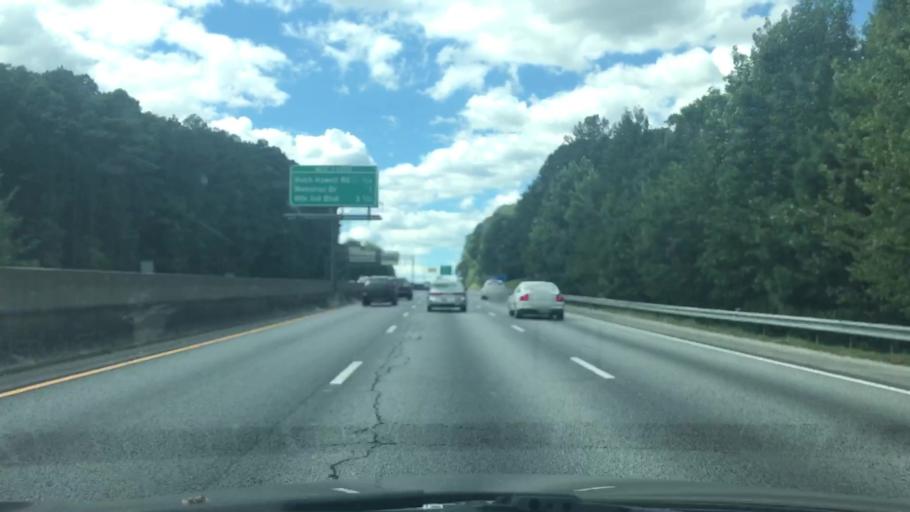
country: US
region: Georgia
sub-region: Gwinnett County
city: Mountain Park
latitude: 33.8238
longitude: -84.1414
